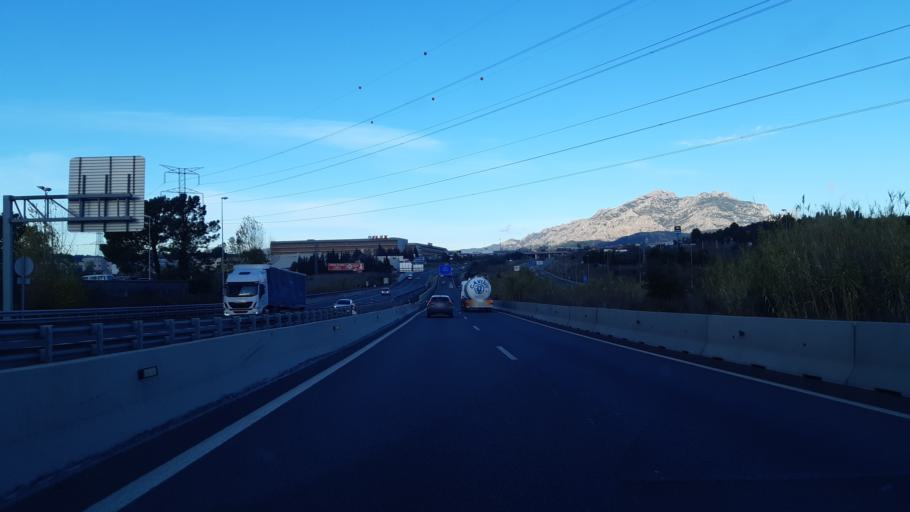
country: ES
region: Catalonia
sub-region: Provincia de Barcelona
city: Abrera
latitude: 41.5233
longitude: 1.8855
